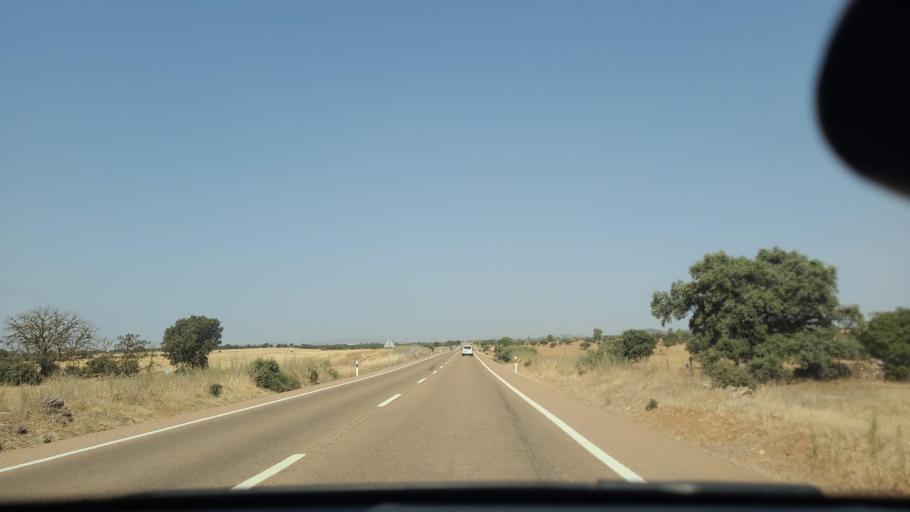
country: ES
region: Extremadura
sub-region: Provincia de Badajoz
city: Usagre
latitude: 38.3694
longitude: -6.2440
